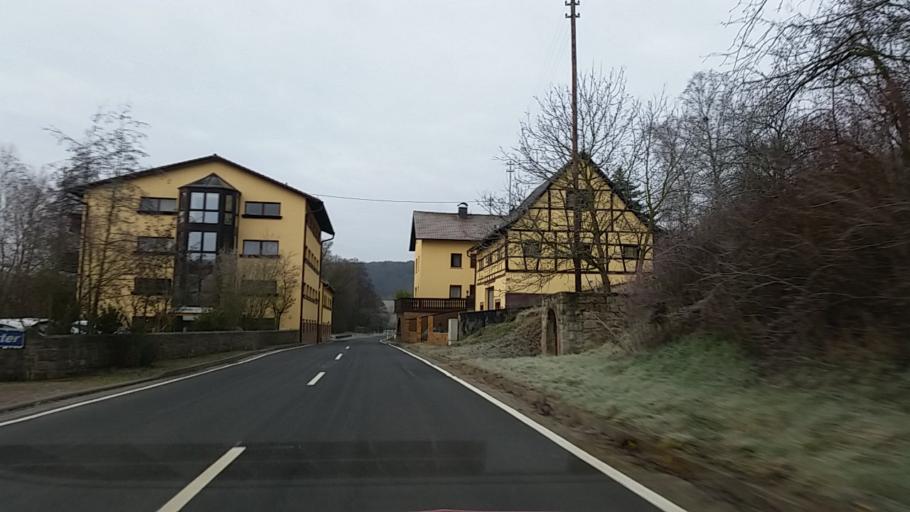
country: DE
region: Bavaria
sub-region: Regierungsbezirk Unterfranken
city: Thungen
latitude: 49.9497
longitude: 9.8328
